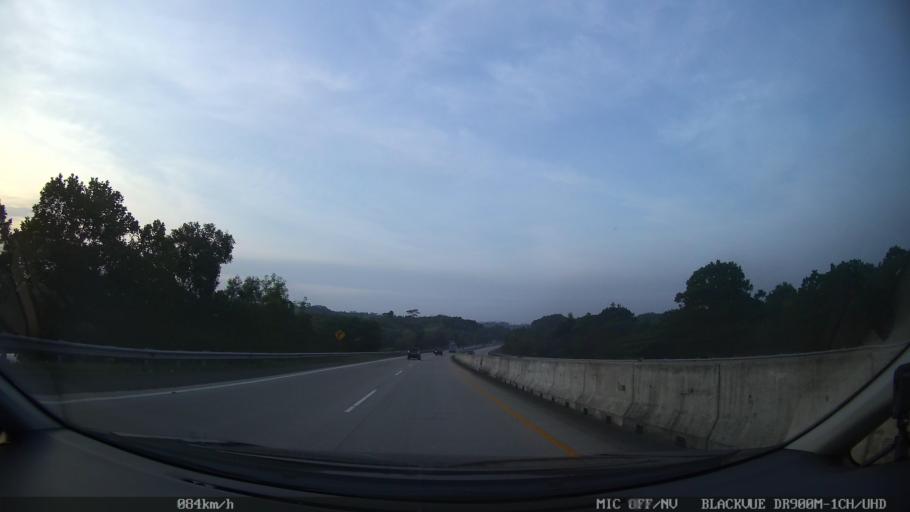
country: ID
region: Lampung
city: Penengahan
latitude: -5.8498
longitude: 105.7280
